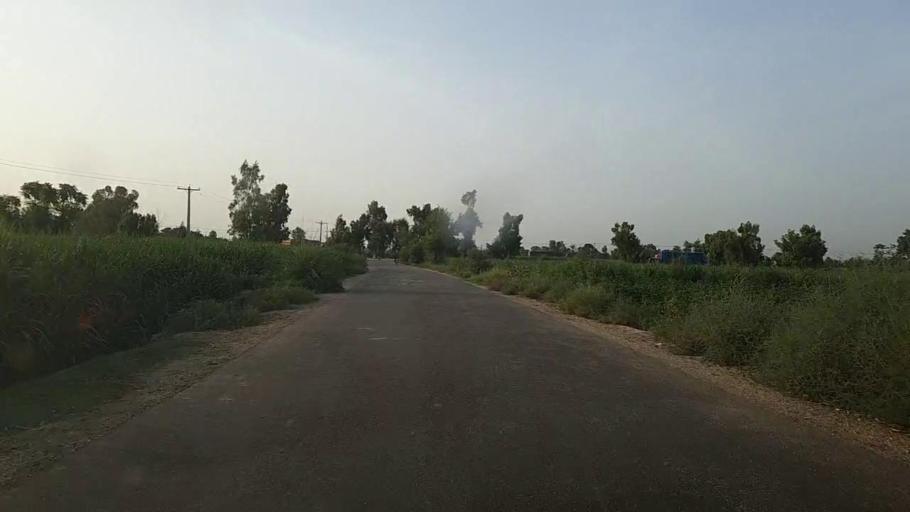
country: PK
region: Sindh
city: Ubauro
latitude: 28.1891
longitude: 69.8273
